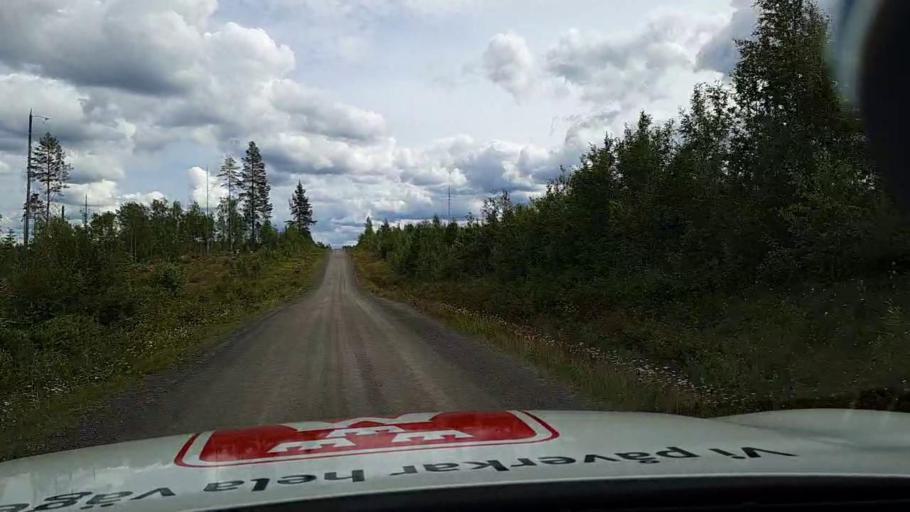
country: SE
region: Jaemtland
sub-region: OEstersunds Kommun
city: Lit
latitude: 63.2955
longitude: 15.3345
